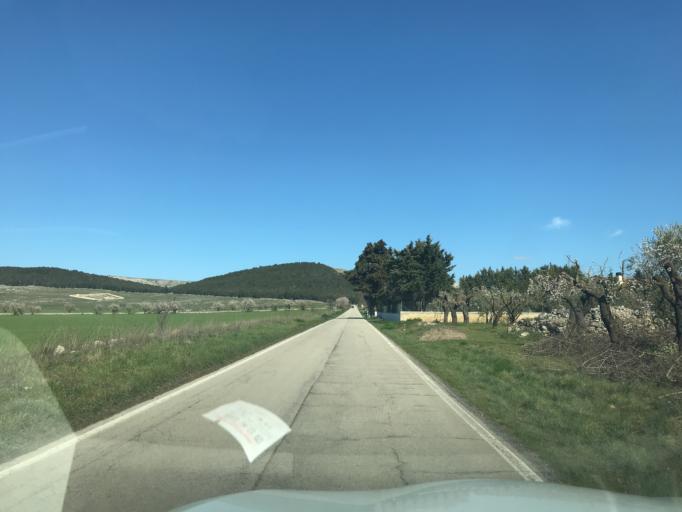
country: IT
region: Apulia
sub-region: Provincia di Bari
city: Gravina in Puglia
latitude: 40.8640
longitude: 16.4387
